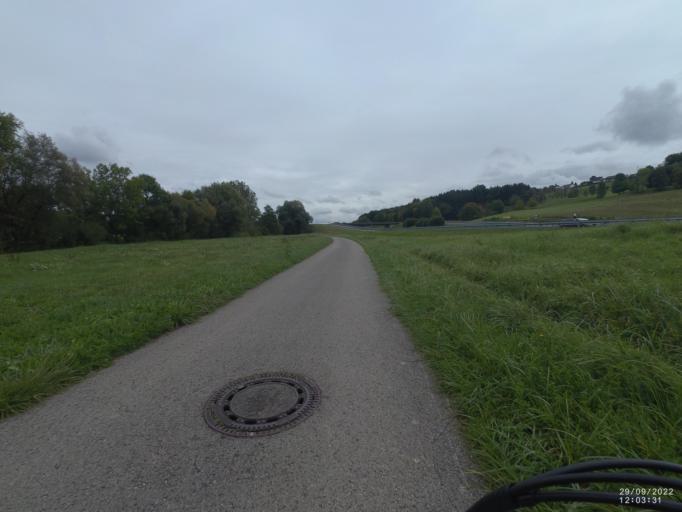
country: DE
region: Baden-Wuerttemberg
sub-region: Regierungsbezirk Stuttgart
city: Ebersbach an der Fils
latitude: 48.7118
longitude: 9.5021
